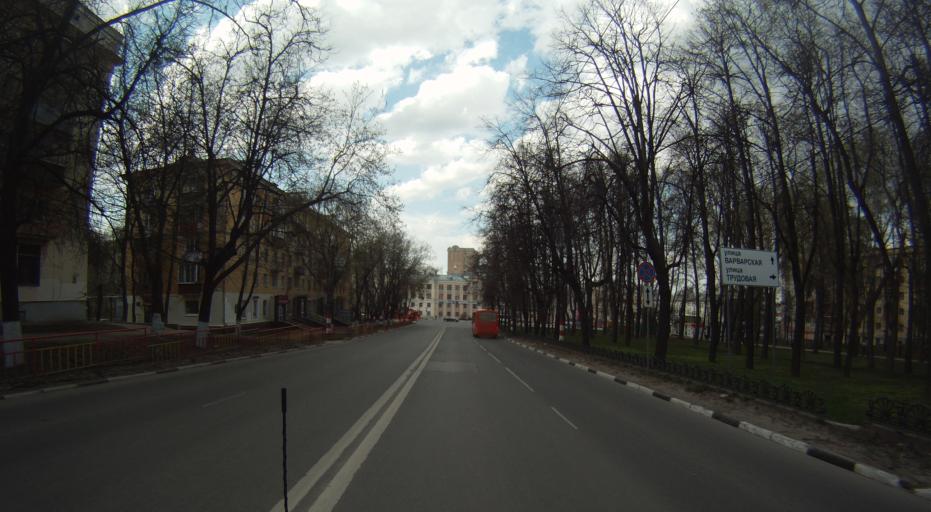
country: RU
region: Nizjnij Novgorod
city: Nizhniy Novgorod
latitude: 56.3169
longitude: 44.0150
